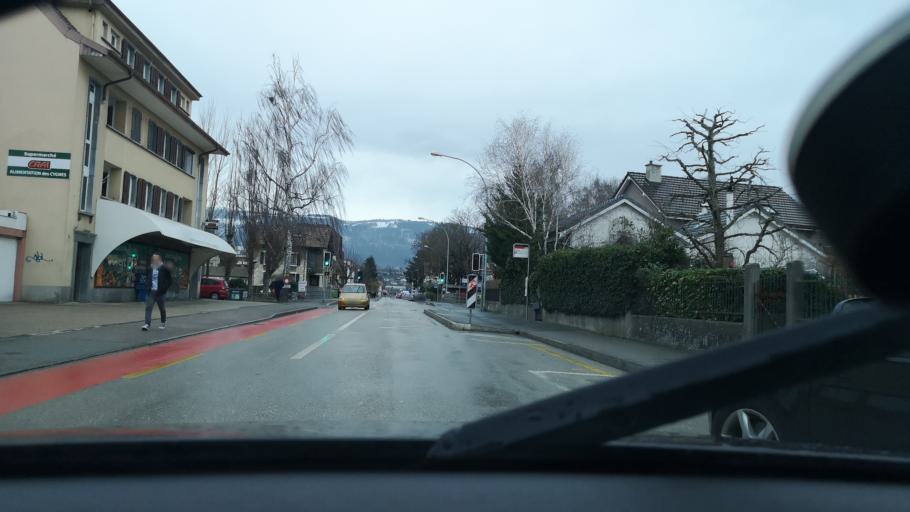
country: CH
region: Vaud
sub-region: Jura-Nord vaudois District
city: Yverdon-les-Bains
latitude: 46.7864
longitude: 6.6353
